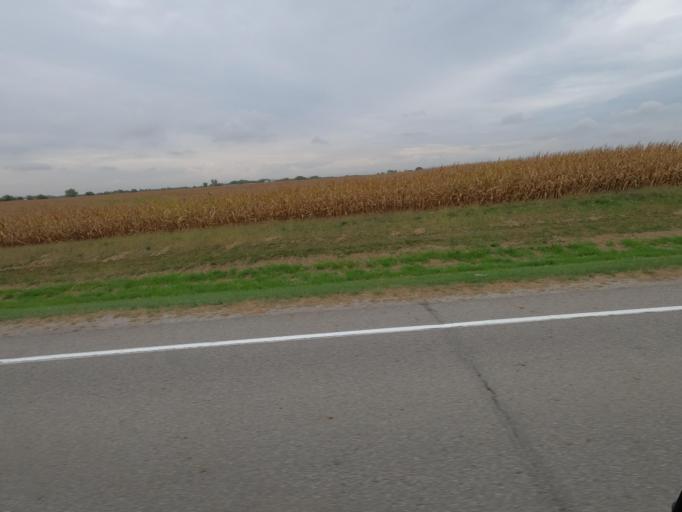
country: US
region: Iowa
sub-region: Van Buren County
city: Keosauqua
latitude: 40.8135
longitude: -91.8875
